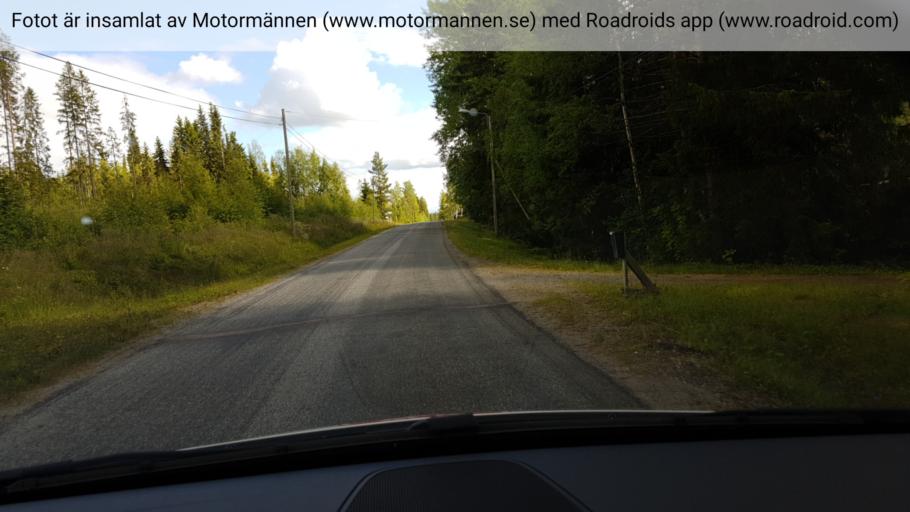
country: SE
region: Vaesterbotten
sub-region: Dorotea Kommun
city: Dorotea
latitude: 64.1054
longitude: 16.3830
